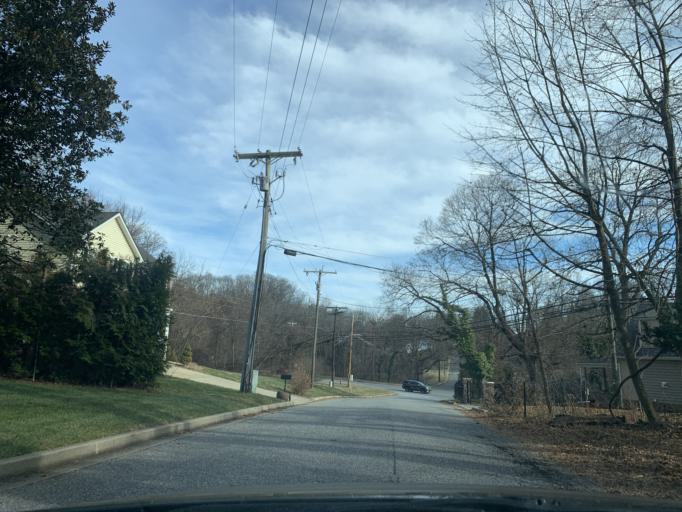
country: US
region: Maryland
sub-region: Baltimore County
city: Pikesville
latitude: 39.3754
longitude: -76.7395
